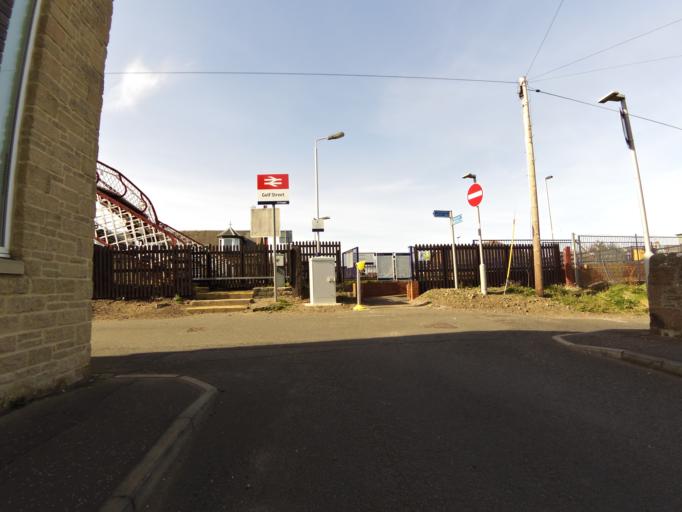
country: GB
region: Scotland
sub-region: Angus
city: Carnoustie
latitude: 56.4977
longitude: -2.7207
